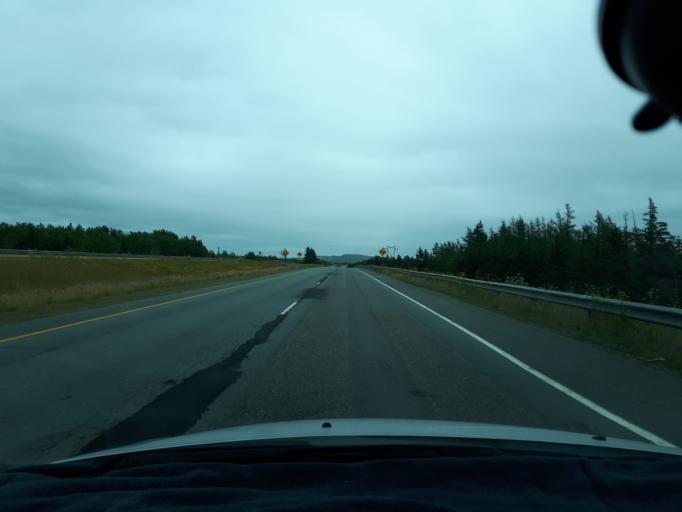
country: CA
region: Nova Scotia
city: Truro
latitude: 45.3944
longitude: -63.3096
